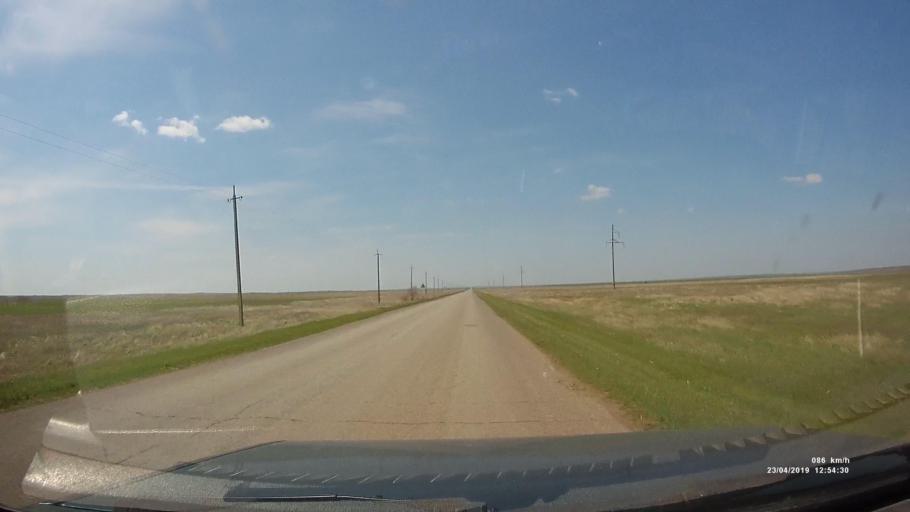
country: RU
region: Kalmykiya
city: Yashalta
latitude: 46.5804
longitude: 42.5777
